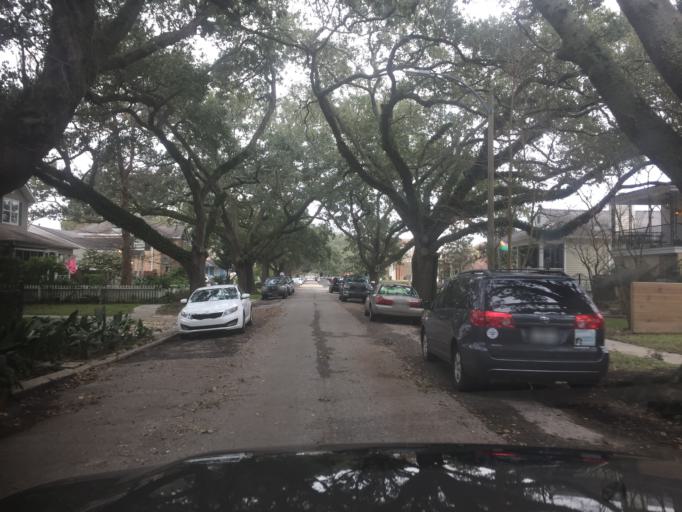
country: US
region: Louisiana
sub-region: Jefferson Parish
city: Metairie
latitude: 29.9962
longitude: -90.1047
